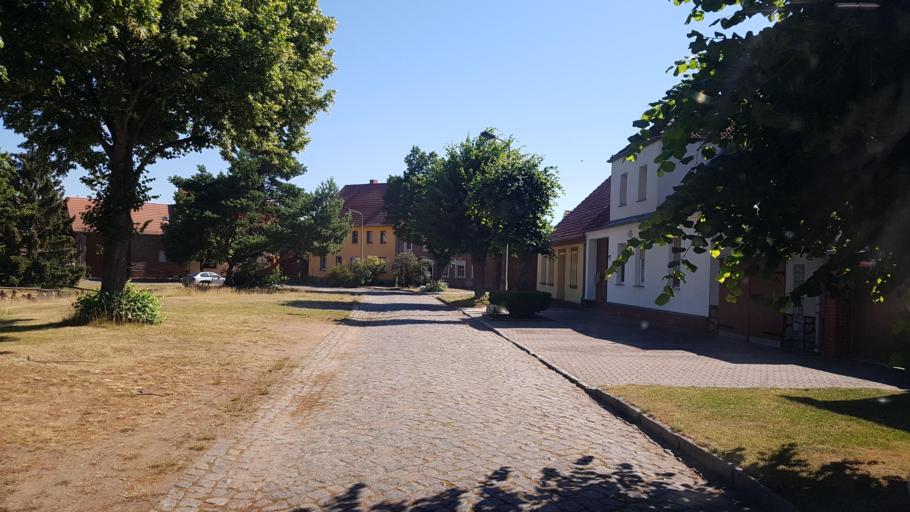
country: DE
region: Brandenburg
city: Juterbog
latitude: 51.9894
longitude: 13.1007
